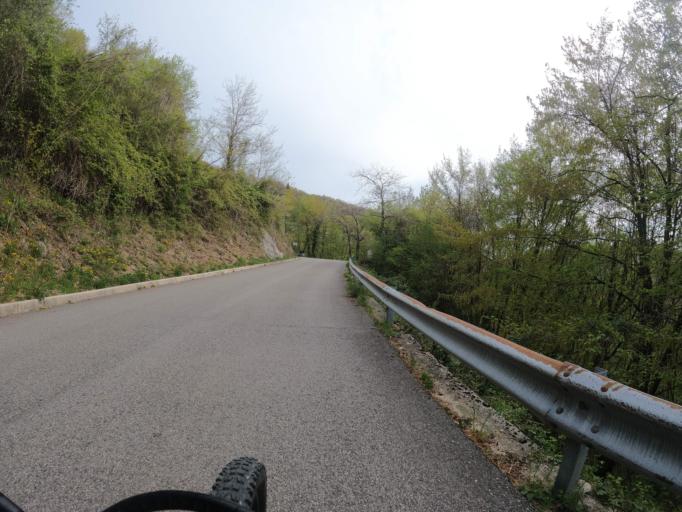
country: IT
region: Friuli Venezia Giulia
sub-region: Provincia di Udine
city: Stregna
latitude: 46.1389
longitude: 13.5767
